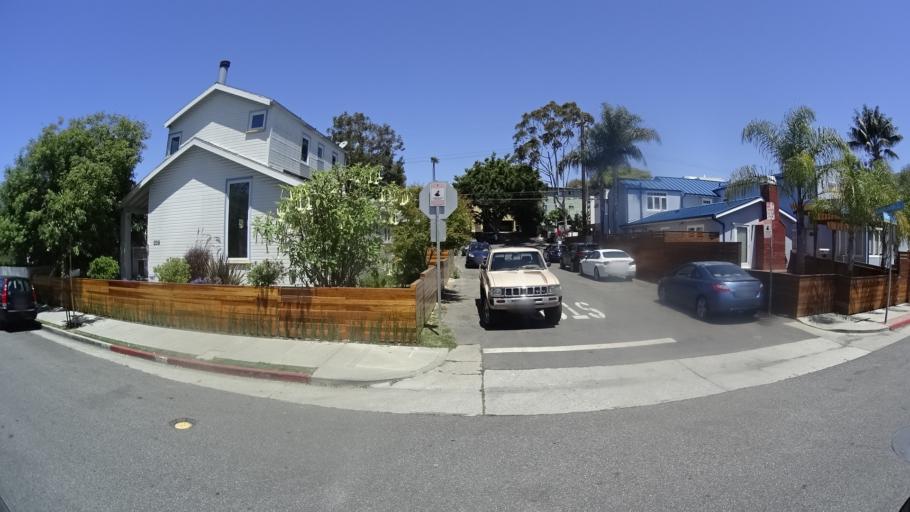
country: US
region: California
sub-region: Los Angeles County
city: Santa Monica
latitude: 34.0020
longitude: -118.4743
